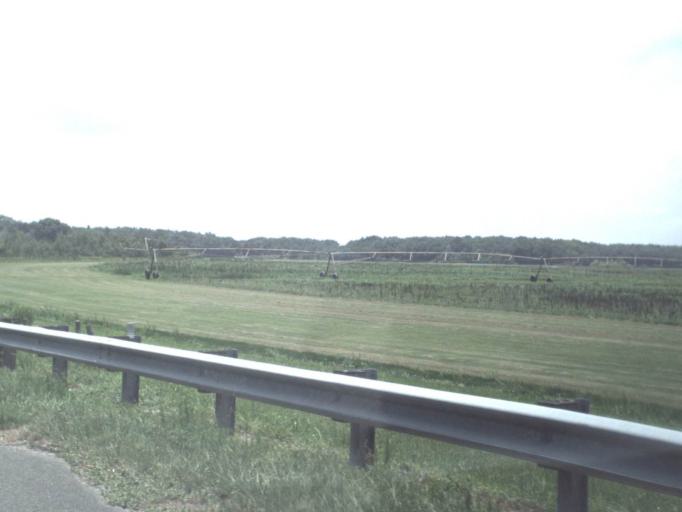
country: US
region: Florida
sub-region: Nassau County
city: Nassau Village-Ratliff
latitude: 30.5116
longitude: -81.7583
